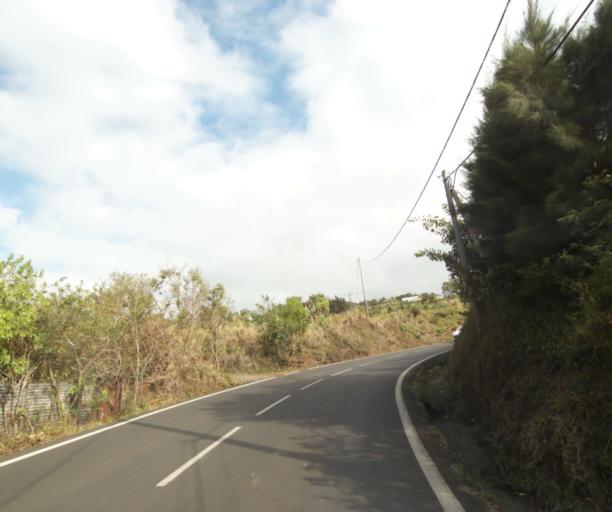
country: RE
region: Reunion
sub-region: Reunion
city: Saint-Paul
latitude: -21.0135
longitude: 55.3194
